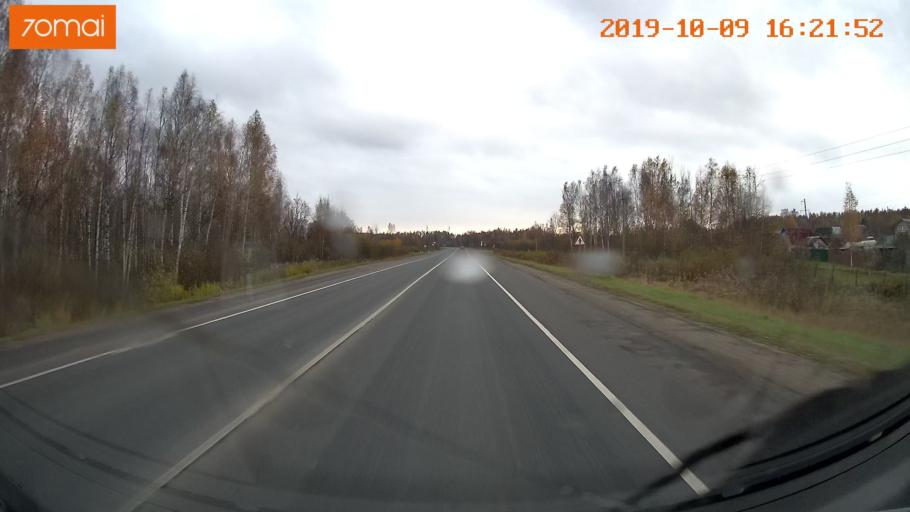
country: RU
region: Kostroma
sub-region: Kostromskoy Rayon
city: Kostroma
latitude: 57.6855
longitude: 40.8878
